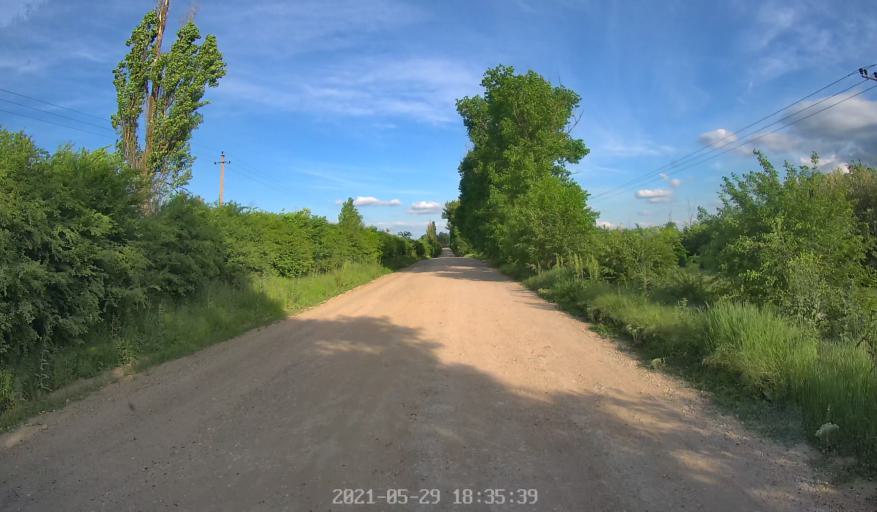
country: MD
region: Chisinau
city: Singera
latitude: 46.8087
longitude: 28.9206
